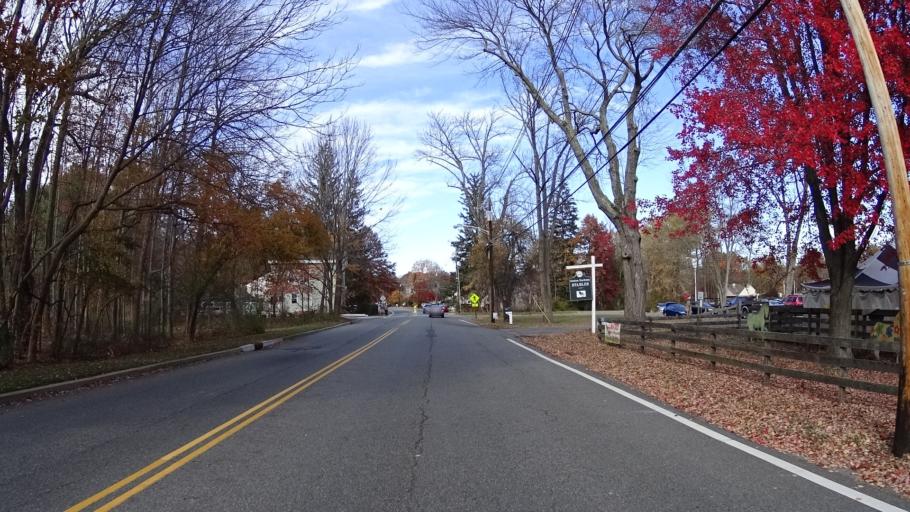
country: US
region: New Jersey
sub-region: Morris County
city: Morristown
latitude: 40.7767
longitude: -74.4670
